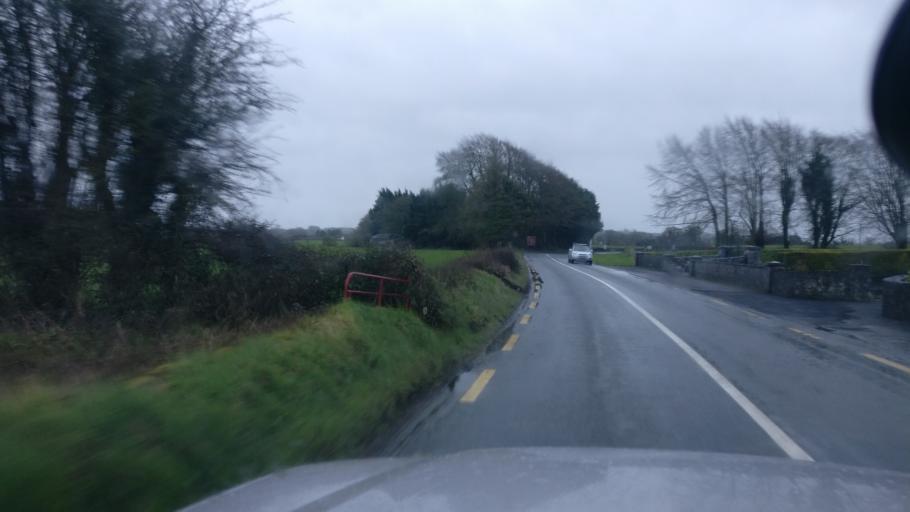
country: IE
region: Connaught
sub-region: County Galway
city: Ballinasloe
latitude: 53.2430
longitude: -8.1720
